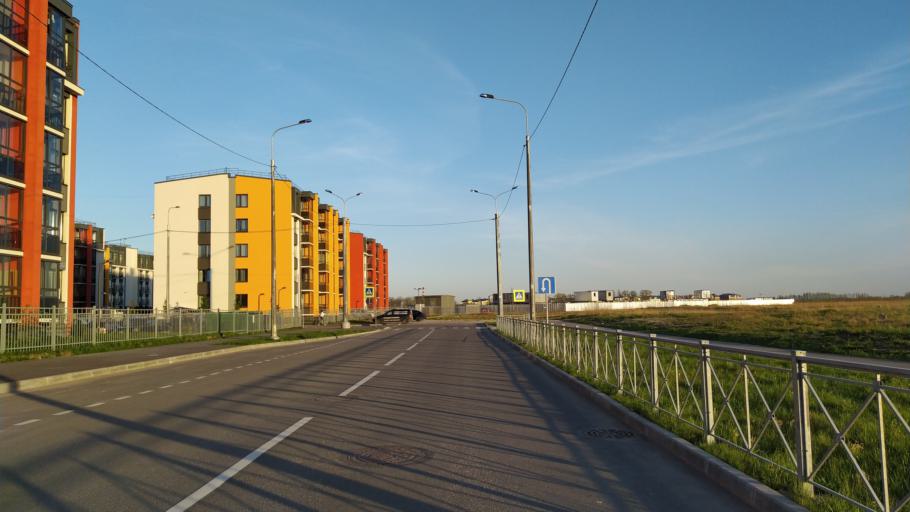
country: RU
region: St.-Petersburg
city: Pushkin
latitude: 59.6977
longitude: 30.4051
